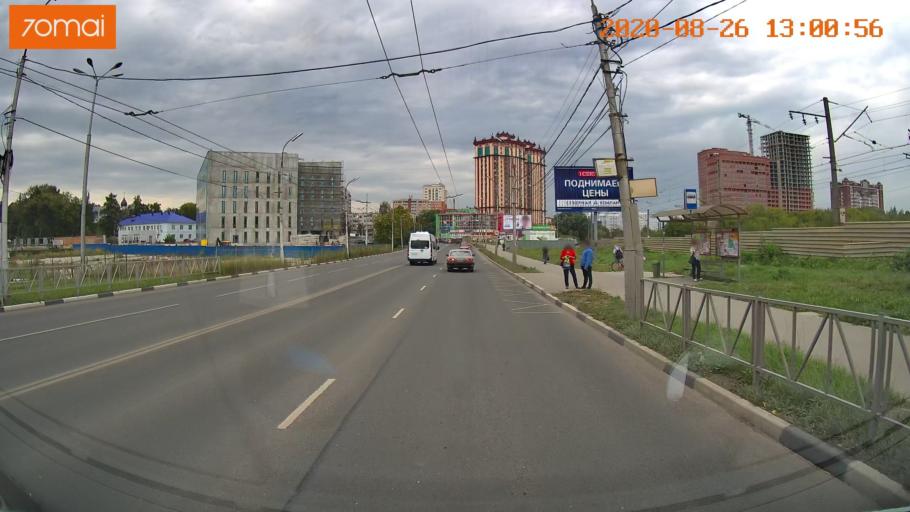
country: RU
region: Rjazan
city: Ryazan'
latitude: 54.6170
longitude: 39.7378
